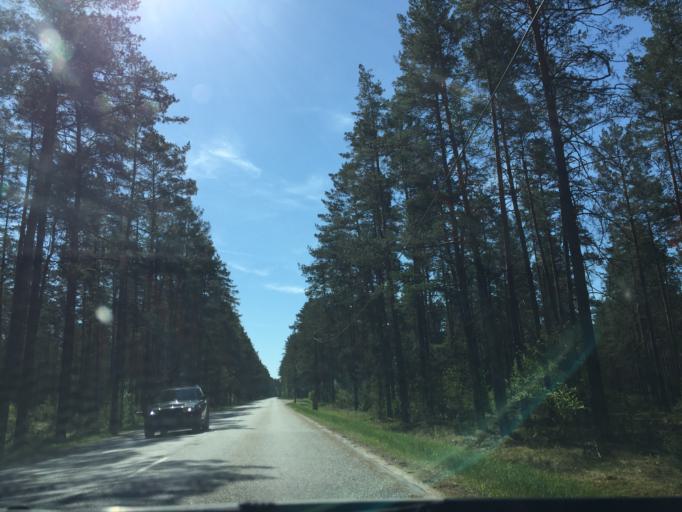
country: LV
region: Garkalne
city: Garkalne
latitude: 57.0308
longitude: 24.4249
